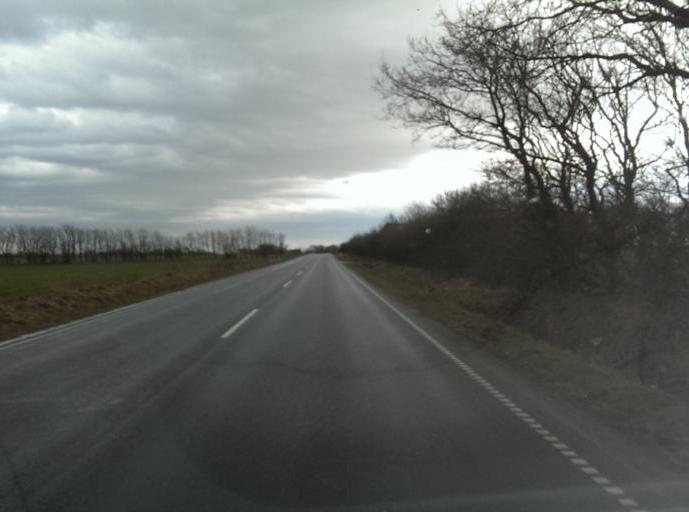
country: DK
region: South Denmark
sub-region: Esbjerg Kommune
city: Tjaereborg
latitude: 55.5112
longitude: 8.5950
